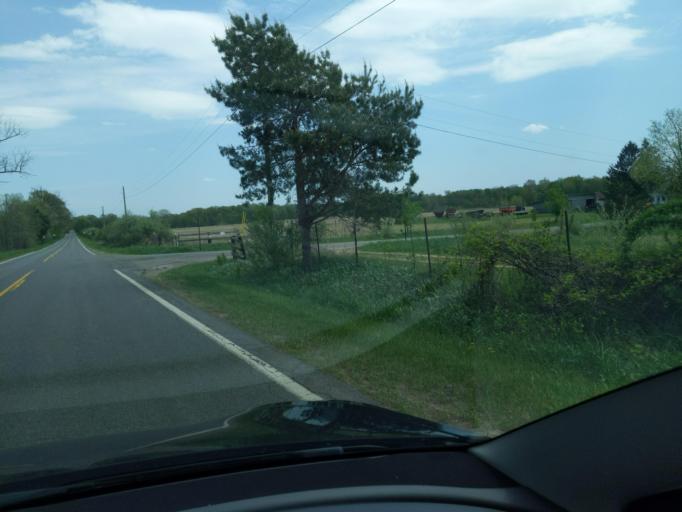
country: US
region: Michigan
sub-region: Ingham County
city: Stockbridge
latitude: 42.4831
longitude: -84.2335
